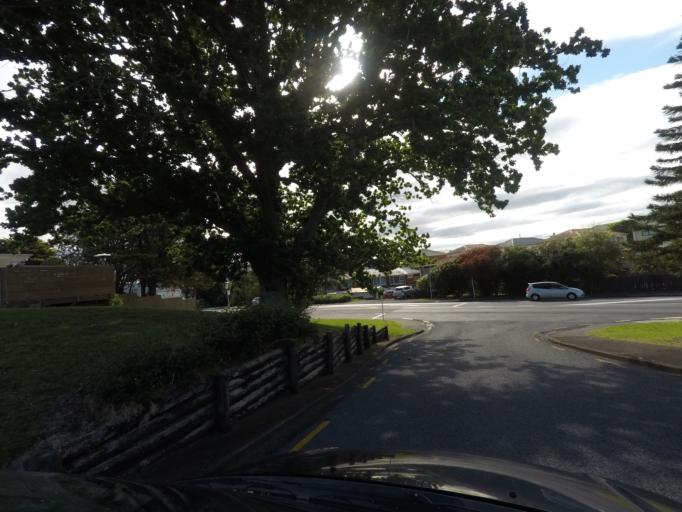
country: NZ
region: Auckland
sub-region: Auckland
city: Rosebank
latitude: -36.8667
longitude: 174.6425
